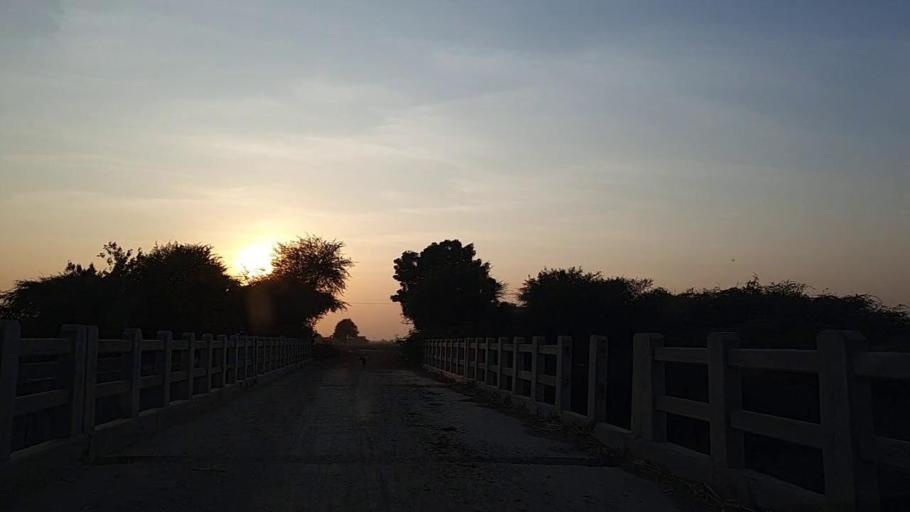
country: PK
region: Sindh
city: Naukot
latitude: 24.9499
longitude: 69.4291
